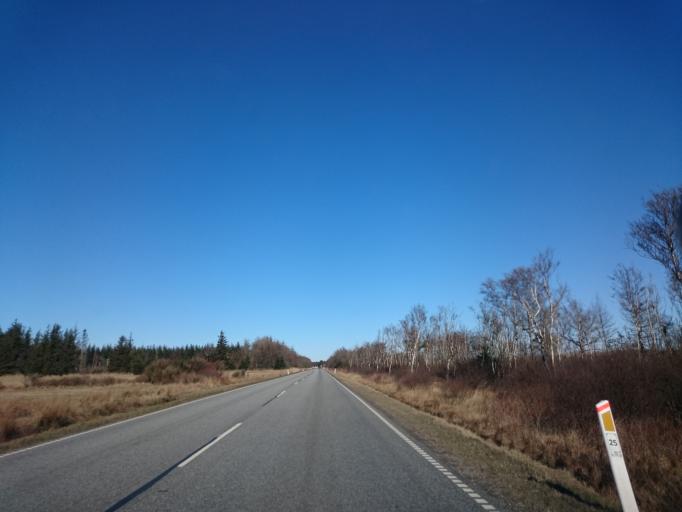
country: DK
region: North Denmark
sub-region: Frederikshavn Kommune
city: Strandby
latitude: 57.6347
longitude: 10.4531
